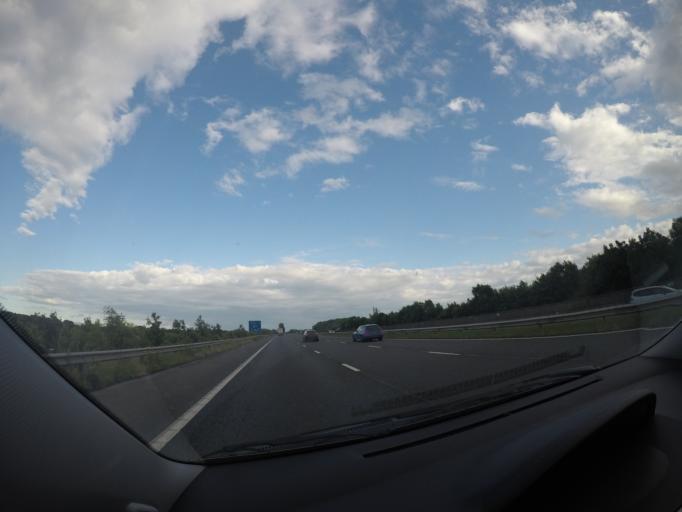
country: GB
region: Scotland
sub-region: Dumfries and Galloway
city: Gretna
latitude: 54.9626
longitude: -2.9937
